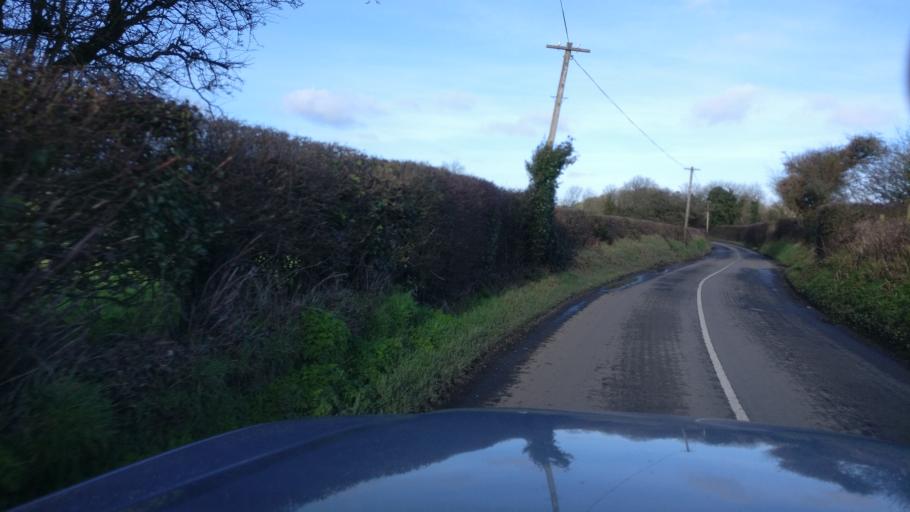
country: IE
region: Leinster
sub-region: Kilkenny
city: Castlecomer
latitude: 52.8826
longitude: -7.1631
